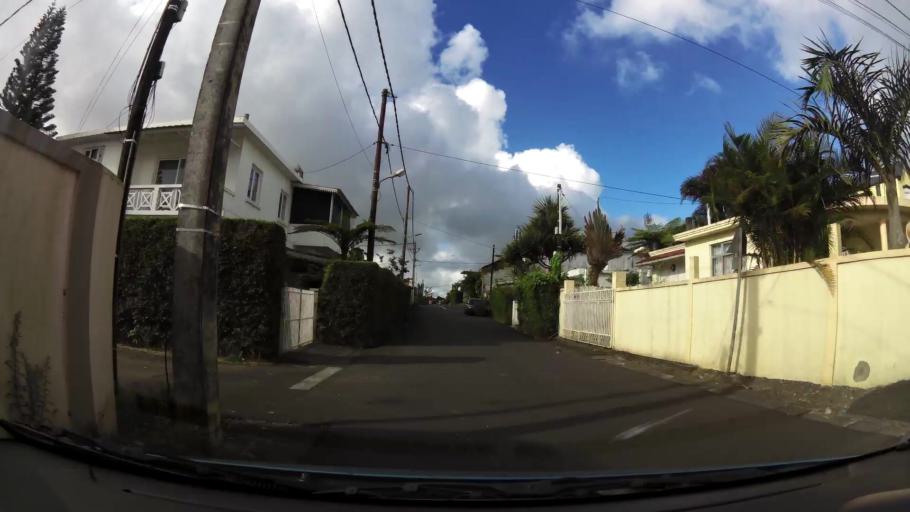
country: MU
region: Plaines Wilhems
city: Curepipe
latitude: -20.3266
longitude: 57.5222
